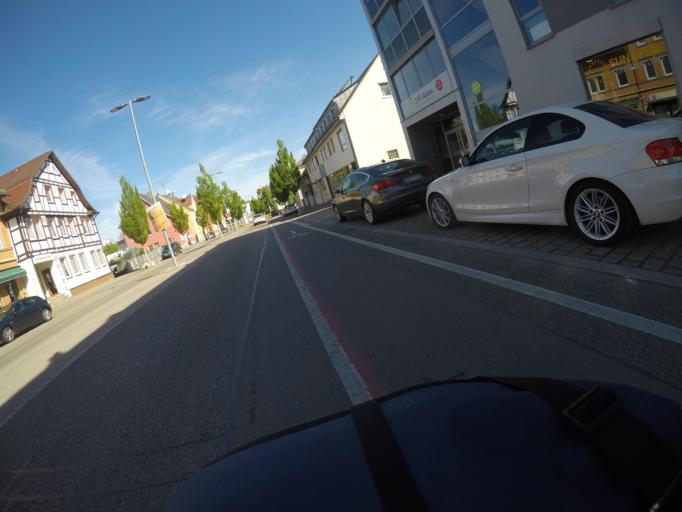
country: DE
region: Baden-Wuerttemberg
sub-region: Regierungsbezirk Stuttgart
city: Aalen
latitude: 48.8425
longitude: 10.0914
